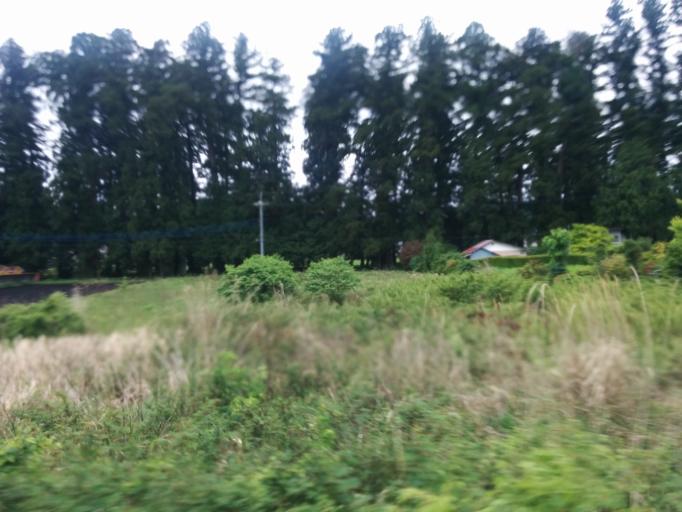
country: JP
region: Tochigi
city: Imaichi
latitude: 36.7141
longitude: 139.6974
